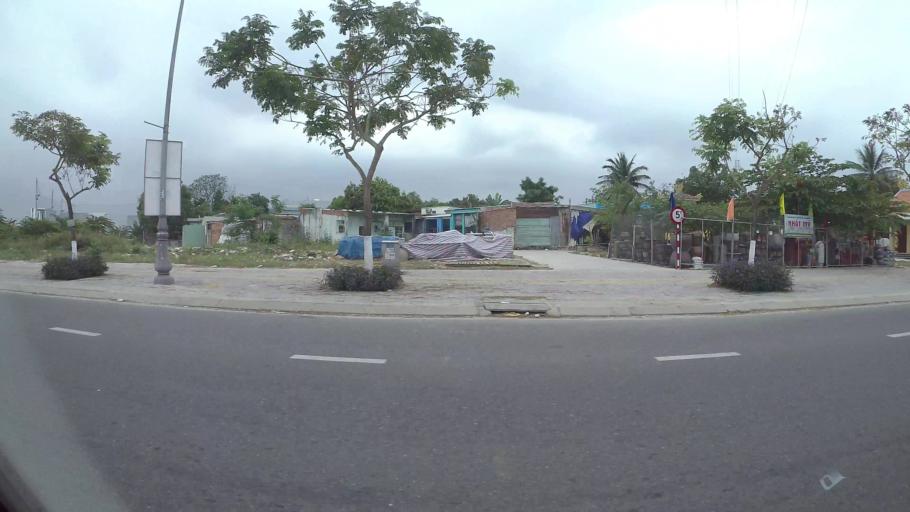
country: VN
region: Da Nang
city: Lien Chieu
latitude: 16.0679
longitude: 108.1697
